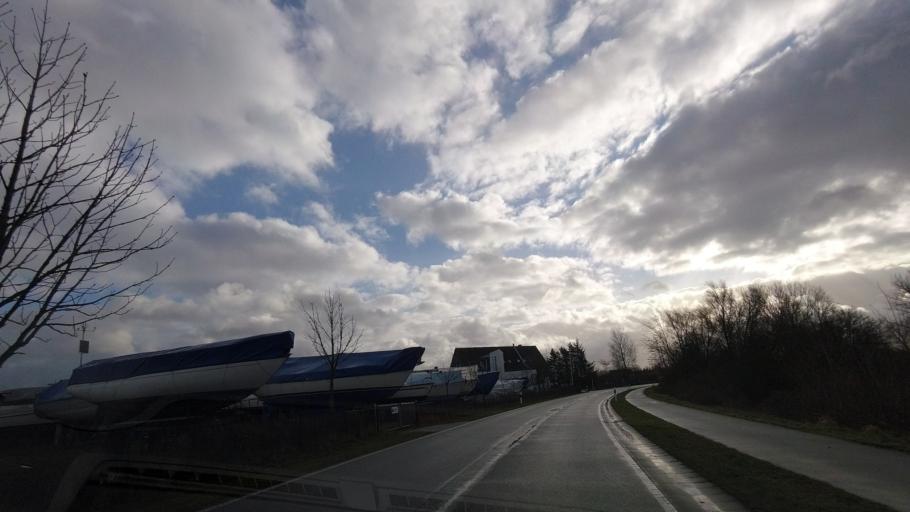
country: DE
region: Schleswig-Holstein
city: Grodersby
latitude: 54.6341
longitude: 9.9274
